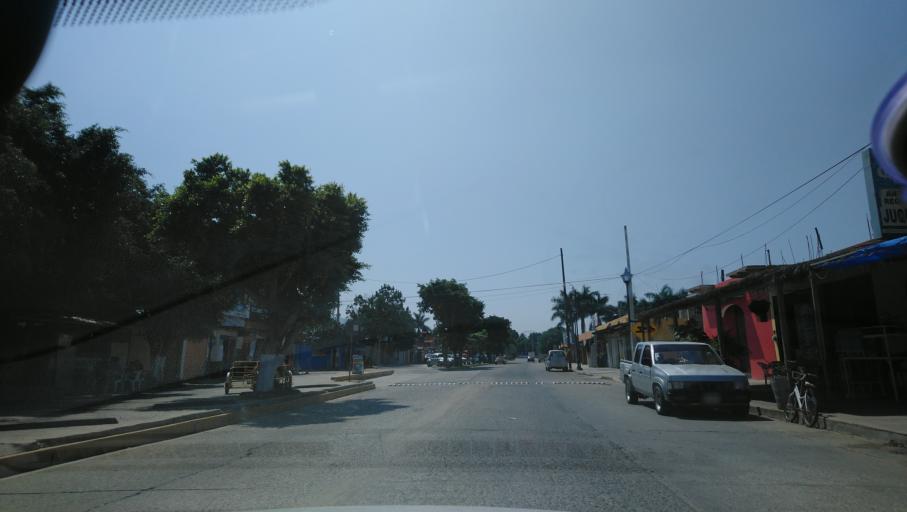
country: MX
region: Oaxaca
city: Santa Maria del Tule
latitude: 17.0451
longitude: -96.6358
